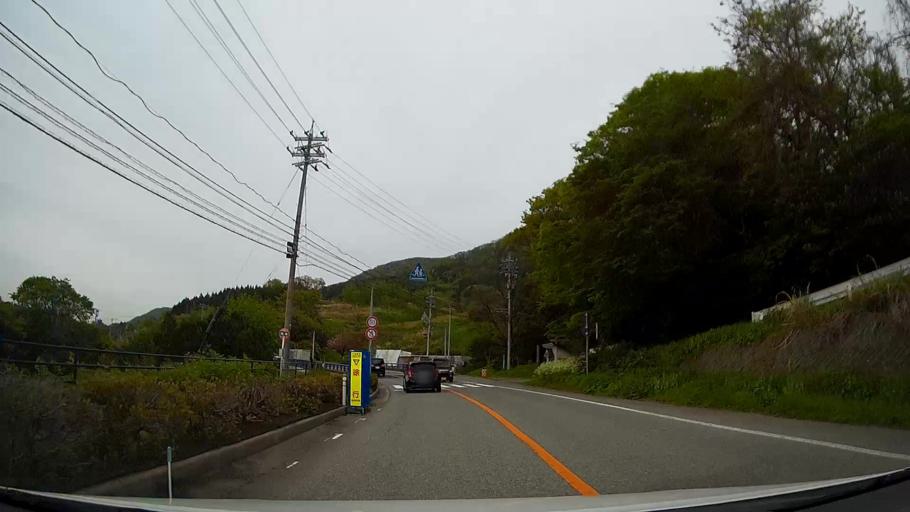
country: JP
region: Ishikawa
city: Nanao
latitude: 37.4021
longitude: 136.9505
